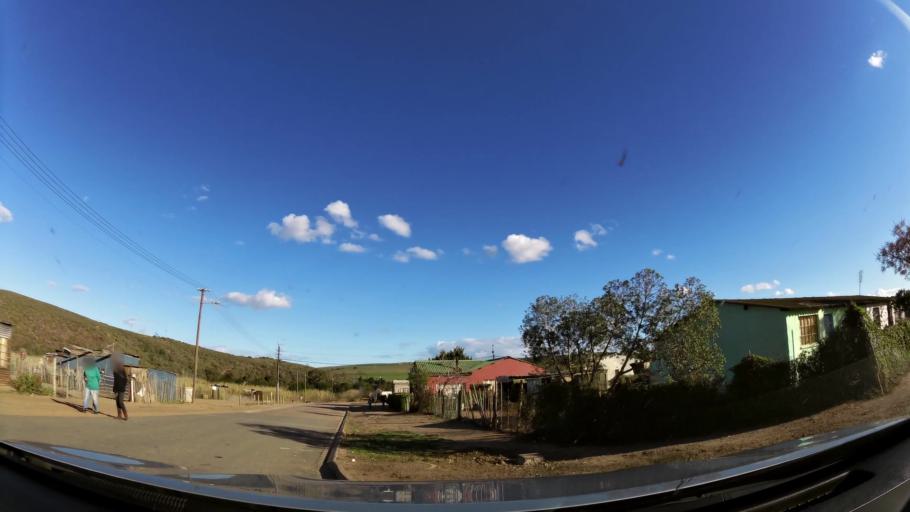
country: ZA
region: Western Cape
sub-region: Eden District Municipality
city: Riversdale
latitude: -34.1058
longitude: 20.9696
